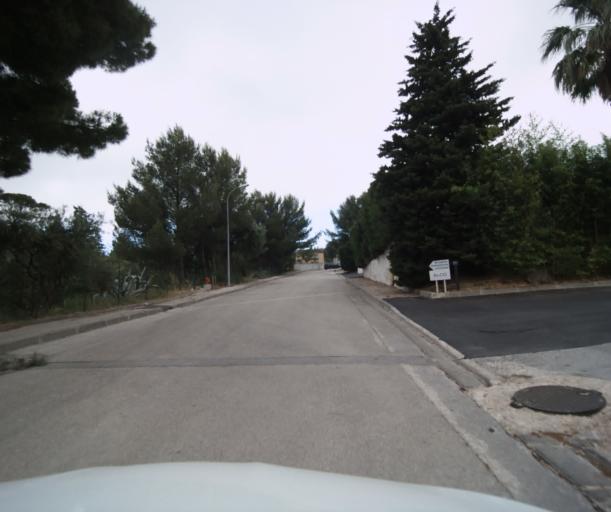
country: FR
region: Provence-Alpes-Cote d'Azur
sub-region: Departement du Var
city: La Seyne-sur-Mer
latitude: 43.1179
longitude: 5.8725
